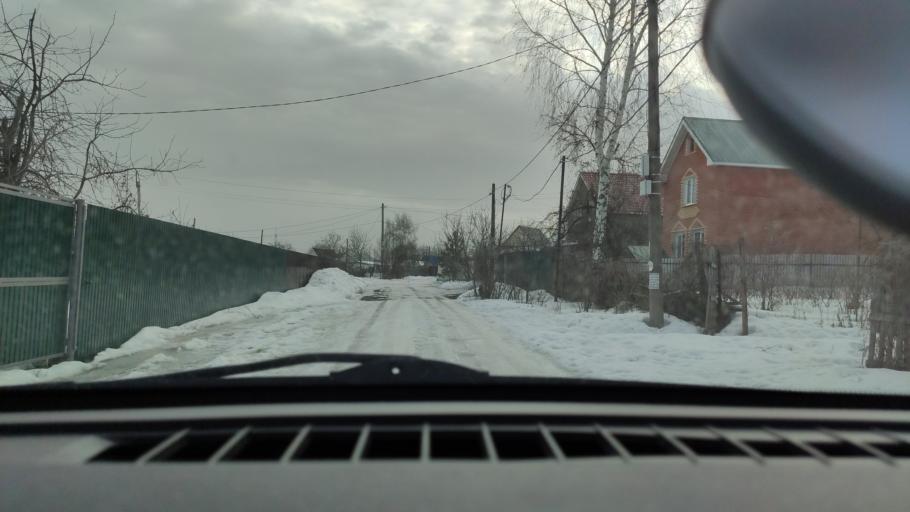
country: RU
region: Samara
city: Petra-Dubrava
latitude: 53.2652
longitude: 50.3059
